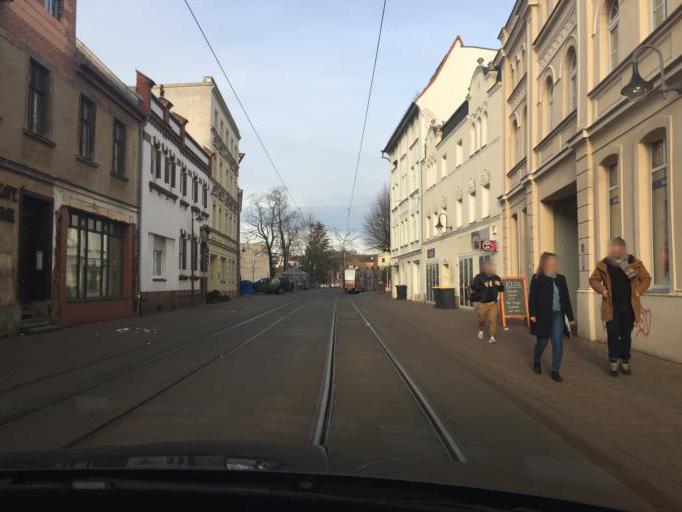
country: DE
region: Brandenburg
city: Cottbus
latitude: 51.7639
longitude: 14.3323
